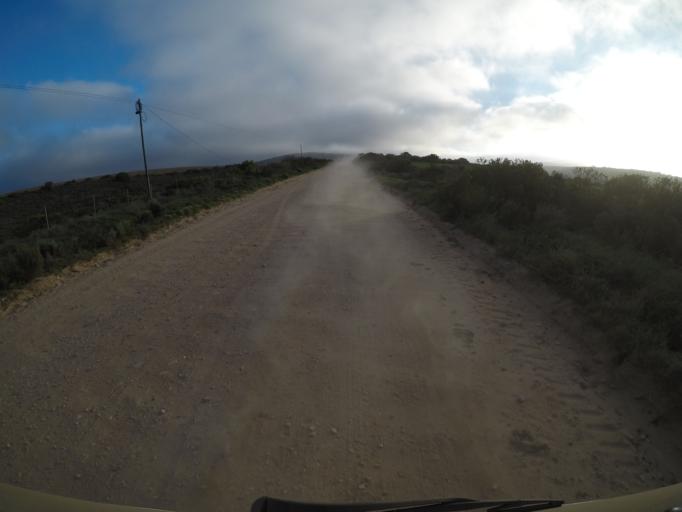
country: ZA
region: Western Cape
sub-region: Eden District Municipality
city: Mossel Bay
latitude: -34.1331
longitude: 22.0441
